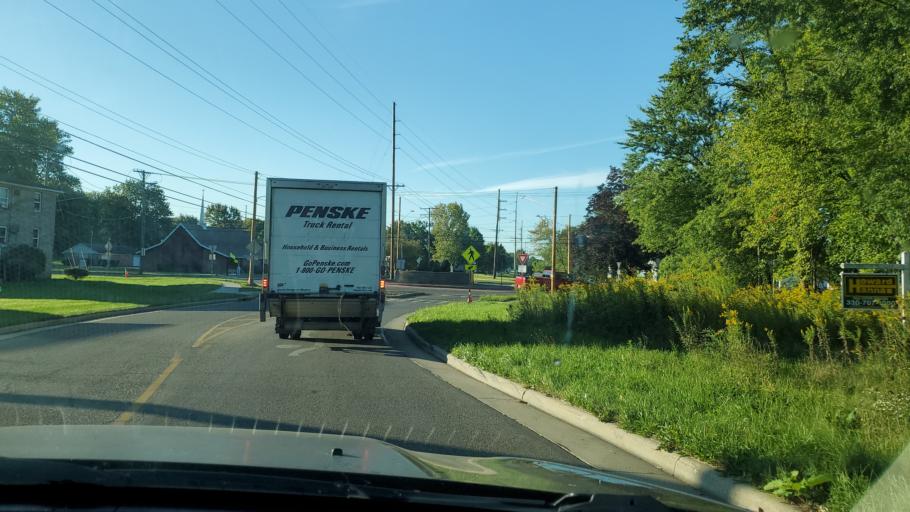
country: US
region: Ohio
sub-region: Mahoning County
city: Poland
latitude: 41.0395
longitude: -80.6212
